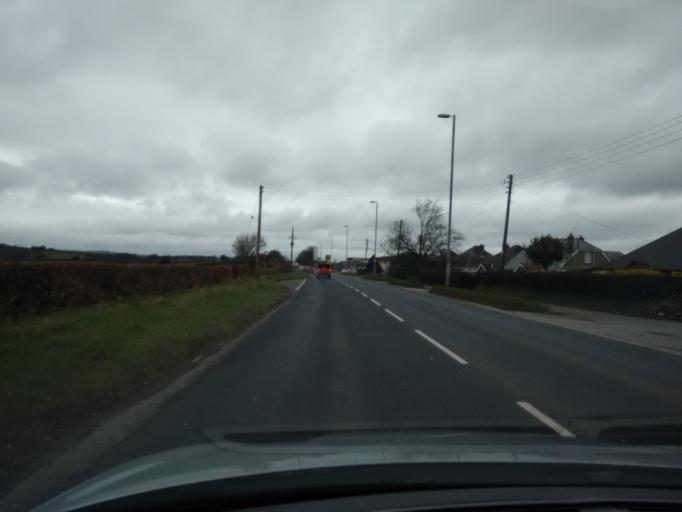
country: GB
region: England
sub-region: Devon
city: Okehampton
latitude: 50.7407
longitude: -3.9695
